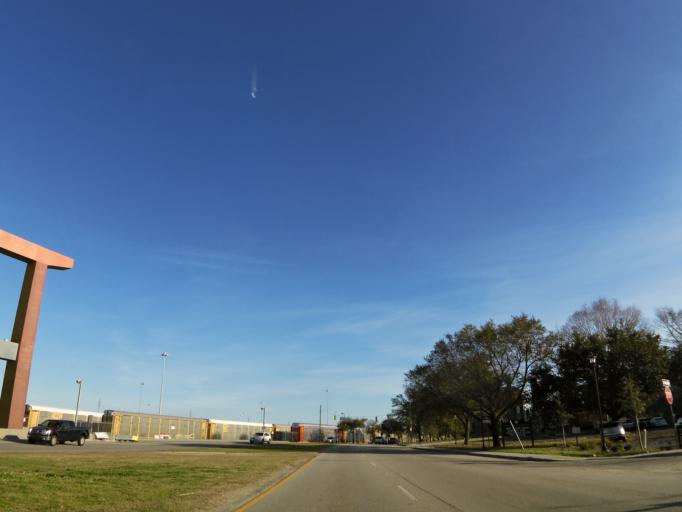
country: US
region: South Carolina
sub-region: Charleston County
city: Charleston
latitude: 32.8003
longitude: -79.9359
